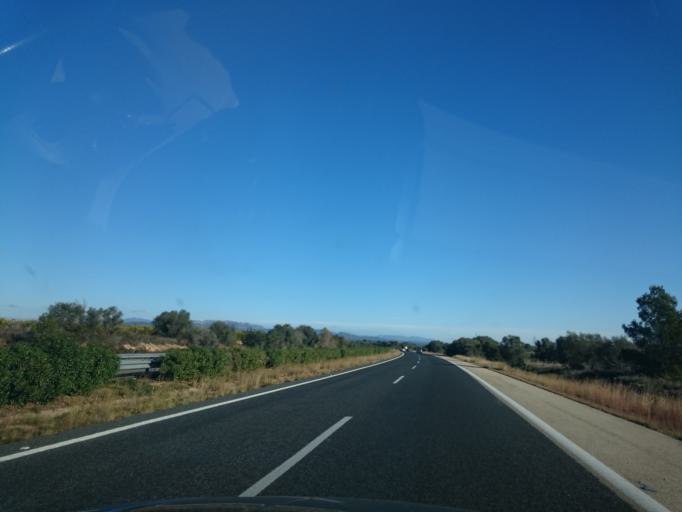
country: ES
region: Catalonia
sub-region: Provincia de Tarragona
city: Masdenverge
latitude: 40.6987
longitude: 0.5418
